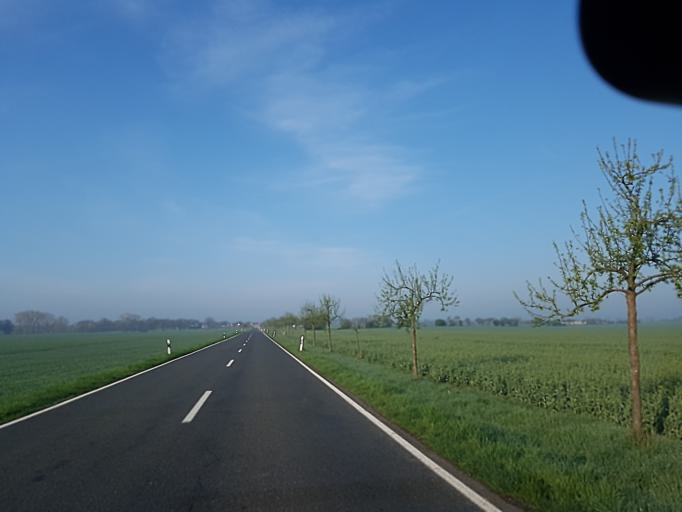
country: DE
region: Saxony
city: Cavertitz
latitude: 51.3699
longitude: 13.0951
